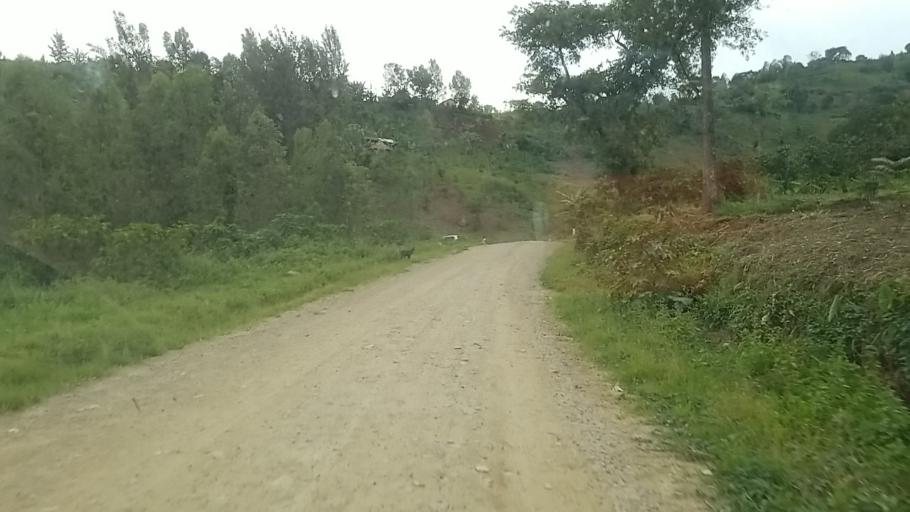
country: CD
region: Nord Kivu
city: Sake
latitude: -1.9608
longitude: 28.9166
